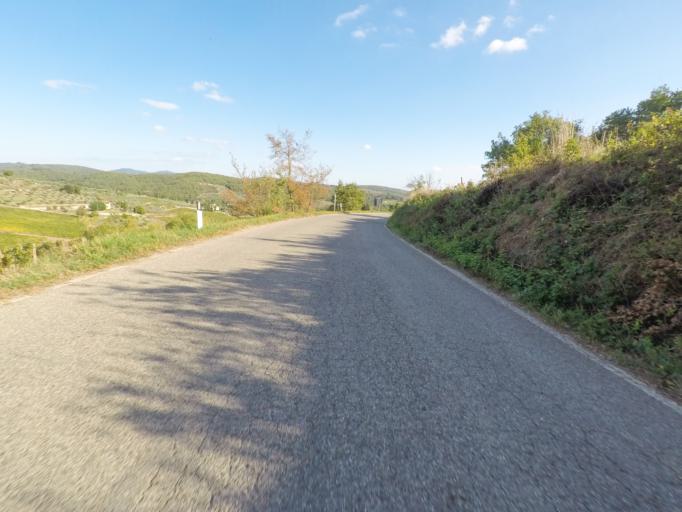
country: IT
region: Tuscany
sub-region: Provincia di Siena
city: Radda in Chianti
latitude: 43.4820
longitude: 11.3667
